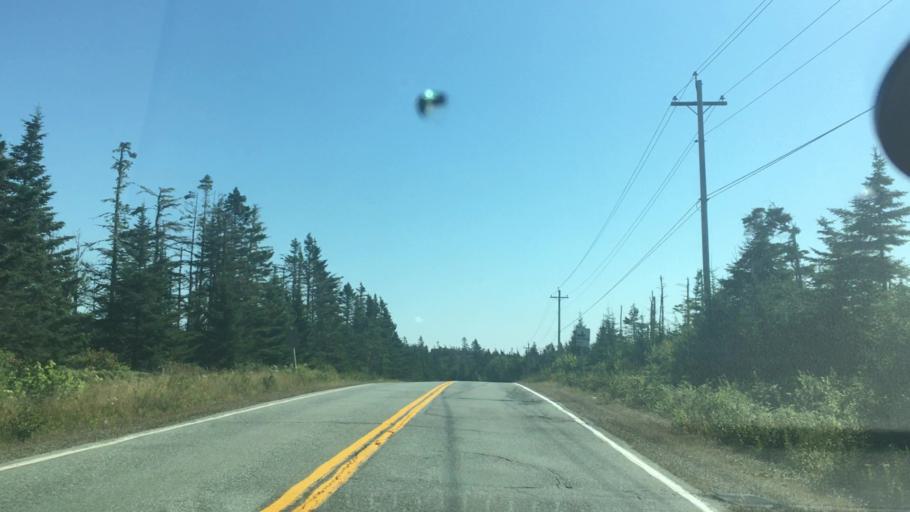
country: CA
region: Nova Scotia
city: New Glasgow
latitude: 44.9176
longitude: -62.3305
